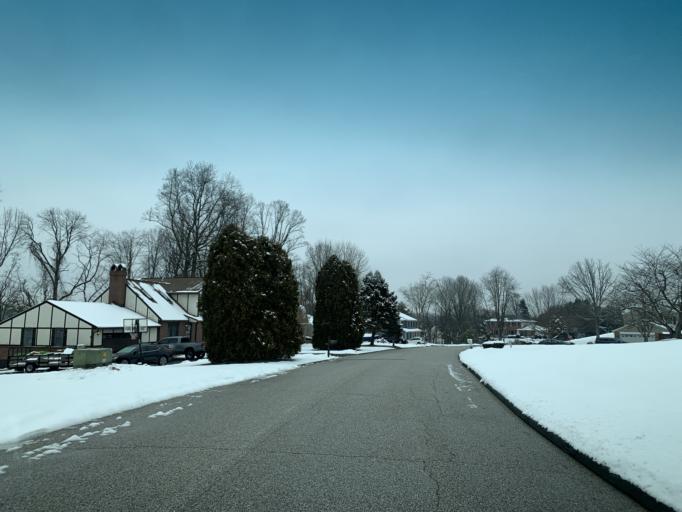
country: US
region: Maryland
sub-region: Harford County
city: Pleasant Hills
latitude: 39.5085
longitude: -76.3781
